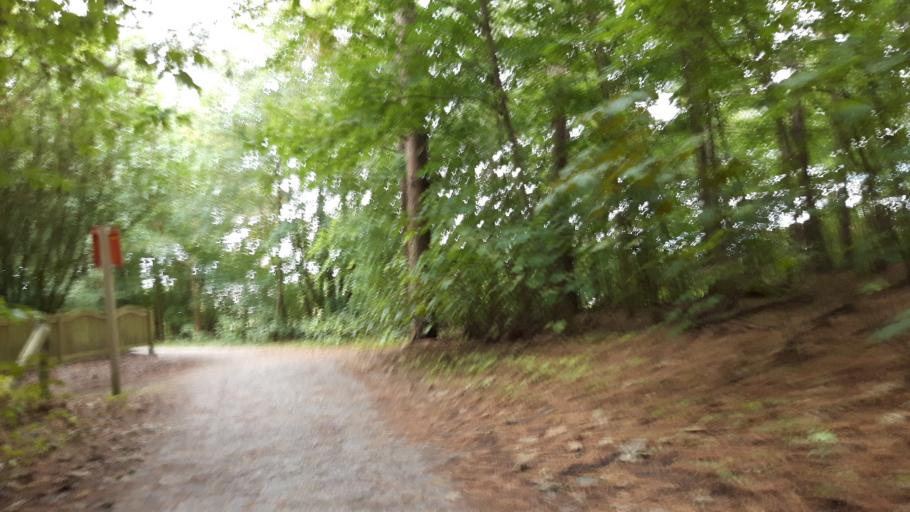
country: NL
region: Friesland
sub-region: Gemeente Ameland
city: Hollum
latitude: 53.4480
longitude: 5.6265
